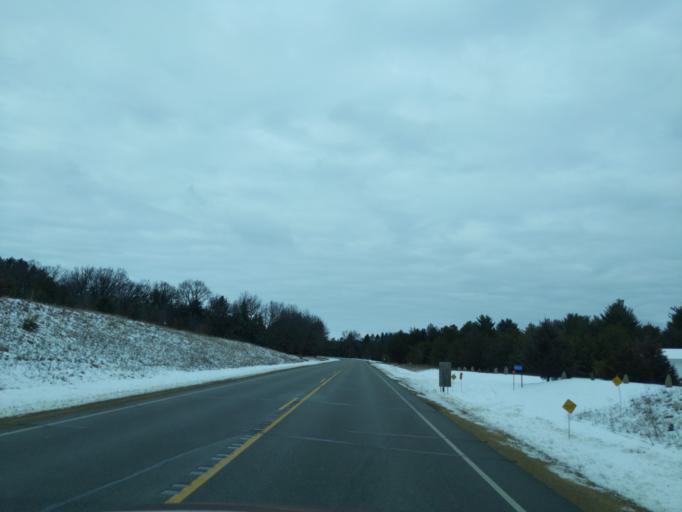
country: US
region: Wisconsin
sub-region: Waushara County
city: Wautoma
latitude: 43.9532
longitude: -89.3173
